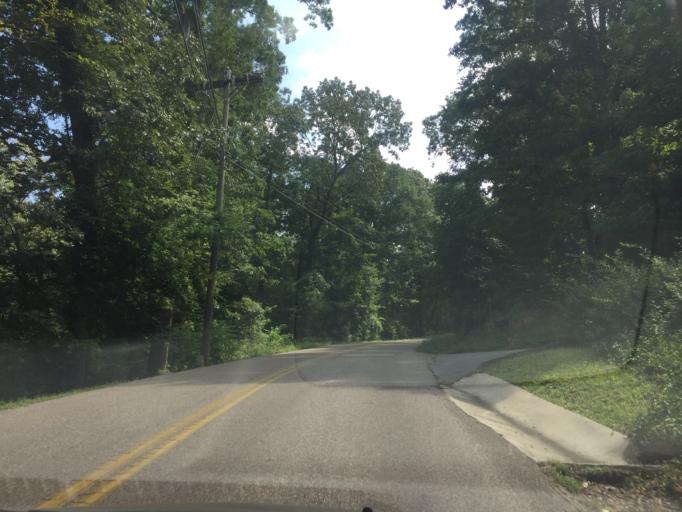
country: US
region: Tennessee
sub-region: Hamilton County
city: Harrison
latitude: 35.0971
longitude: -85.1944
